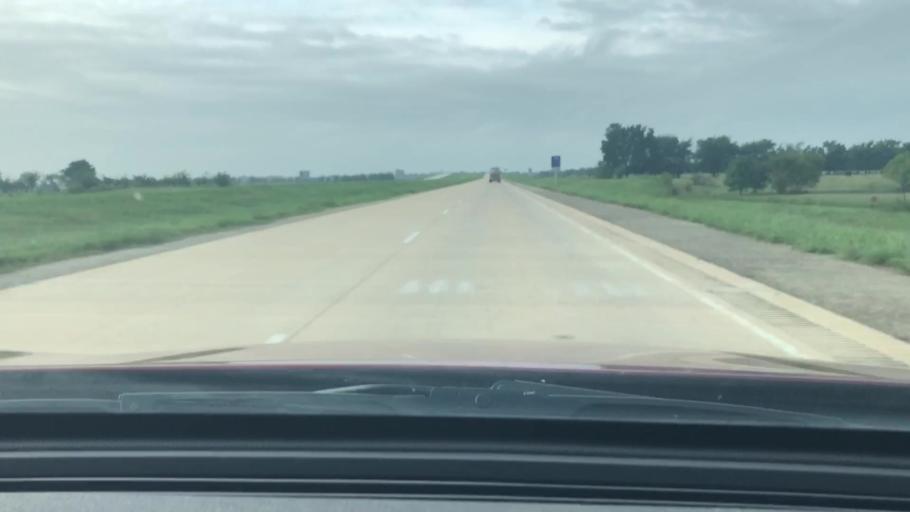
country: US
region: Louisiana
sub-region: Caddo Parish
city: Vivian
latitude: 32.8877
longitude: -93.8603
